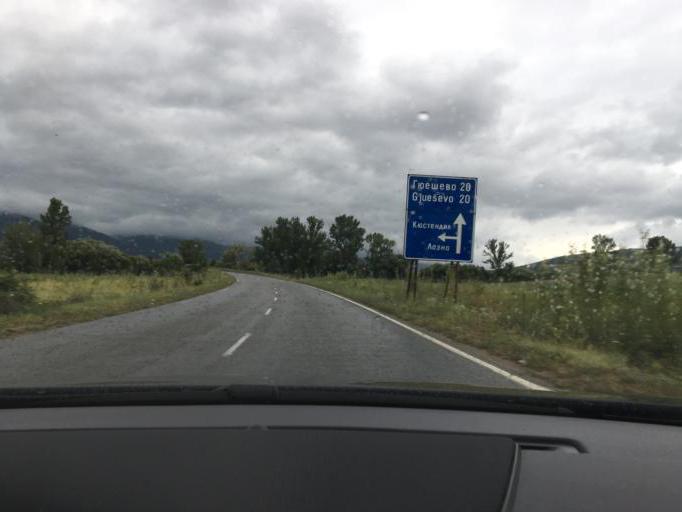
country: BG
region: Kyustendil
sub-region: Obshtina Kyustendil
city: Kyustendil
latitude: 42.2933
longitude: 22.6708
